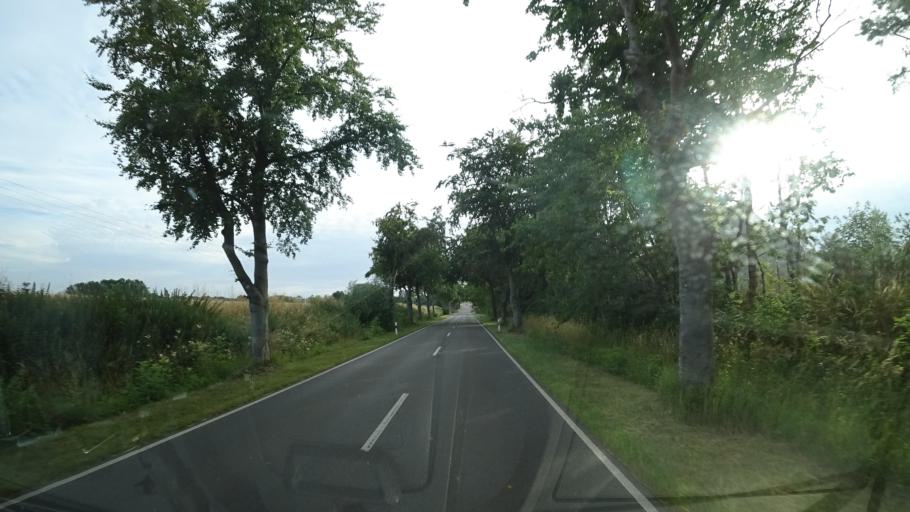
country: DE
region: Mecklenburg-Vorpommern
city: Putbus
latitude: 54.4061
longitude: 13.5118
